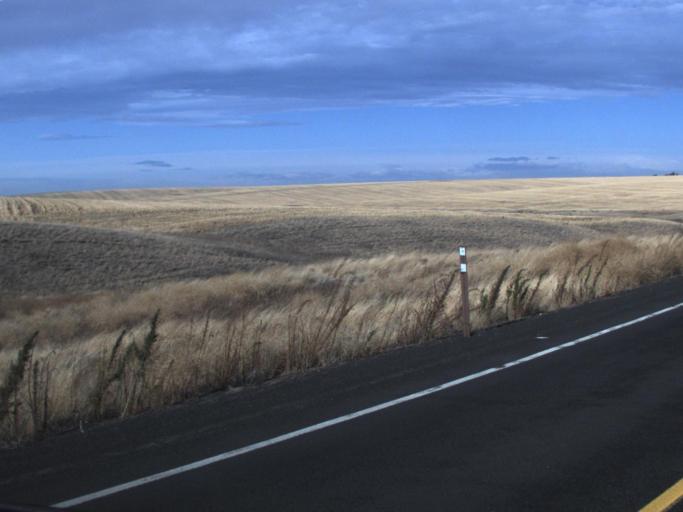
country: US
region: Washington
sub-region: Adams County
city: Ritzville
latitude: 47.1683
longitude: -118.6855
